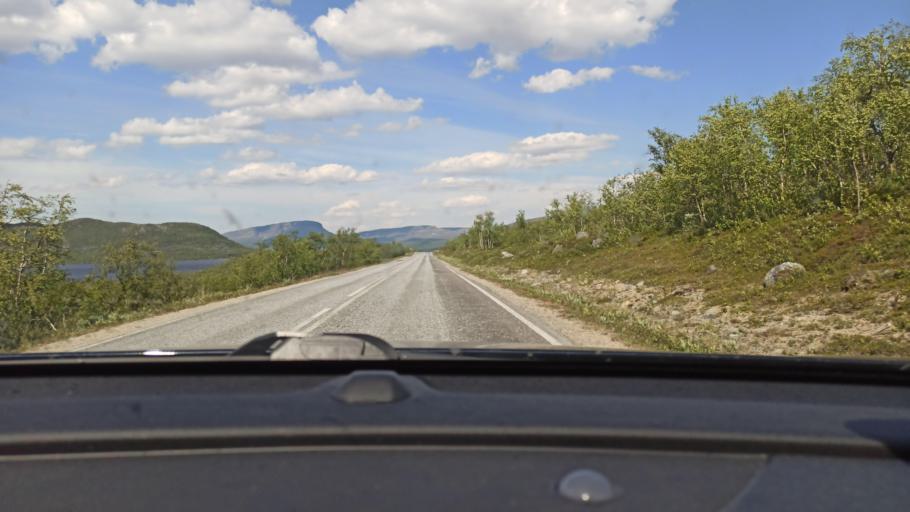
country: NO
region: Troms
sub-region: Kafjord
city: Olderdalen
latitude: 68.9393
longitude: 20.9126
